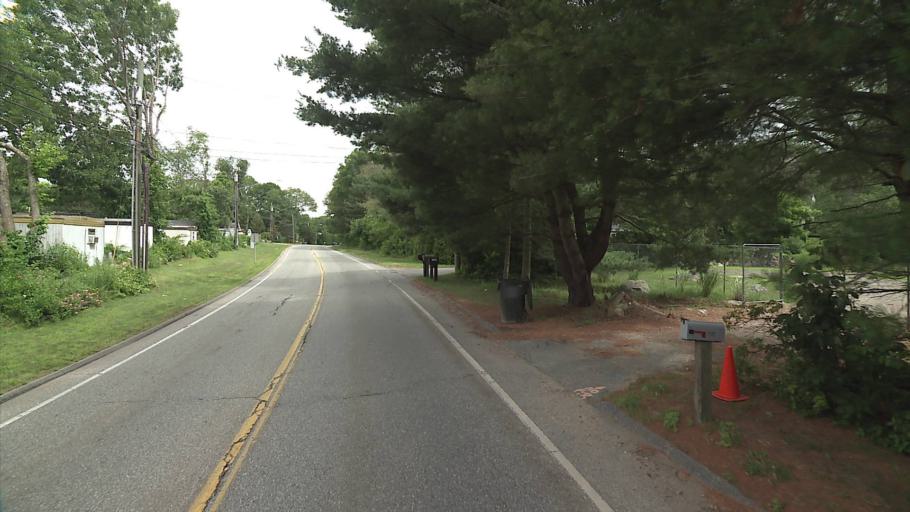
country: US
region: Connecticut
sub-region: New London County
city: Conning Towers-Nautilus Park
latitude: 41.3875
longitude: -72.0273
